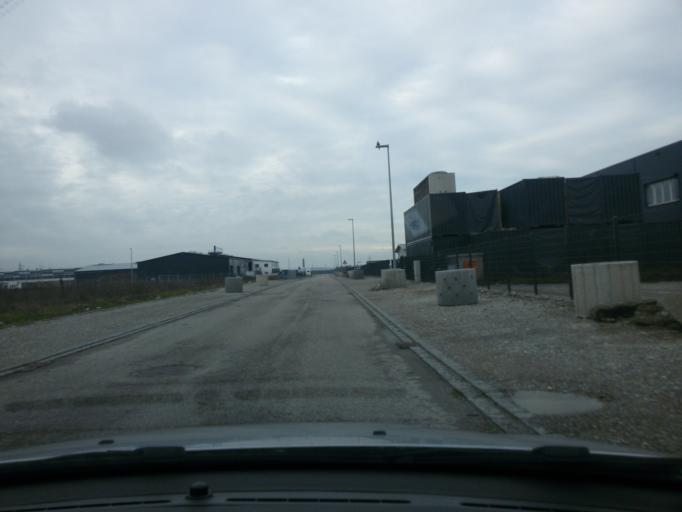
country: DE
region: Bavaria
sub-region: Swabia
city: Kleinaitingen
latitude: 48.2021
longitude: 10.8454
